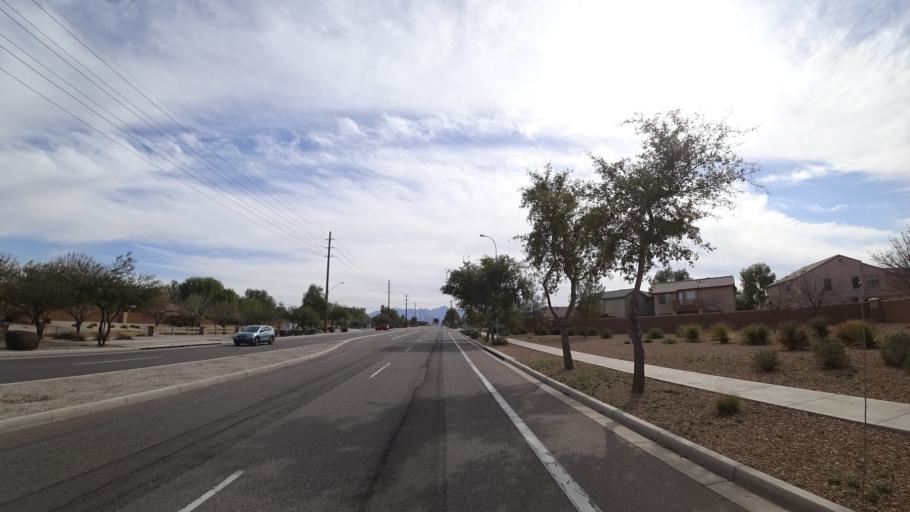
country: US
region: Arizona
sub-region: Maricopa County
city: Tolleson
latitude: 33.4190
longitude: -112.2557
